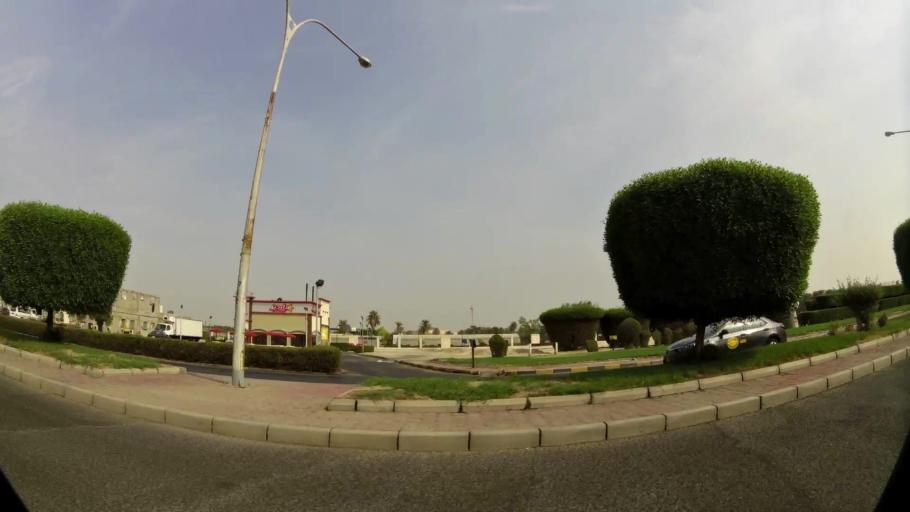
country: KW
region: Al Asimah
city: Ar Rabiyah
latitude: 29.2948
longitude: 47.9390
